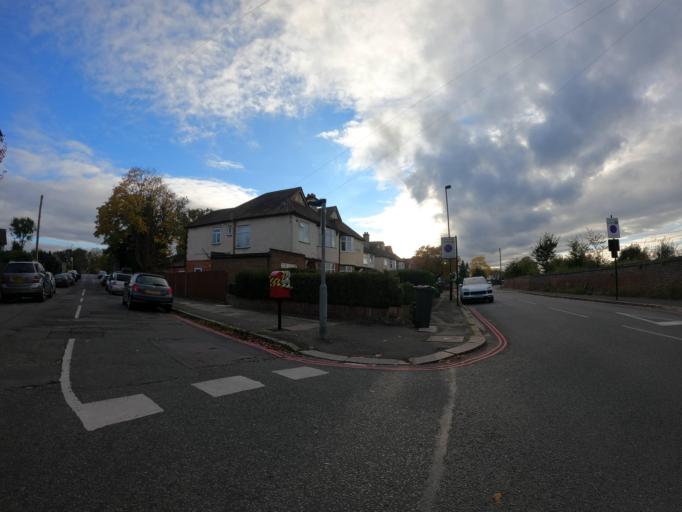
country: GB
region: England
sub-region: Greater London
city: Isleworth
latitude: 51.4852
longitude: -0.3430
